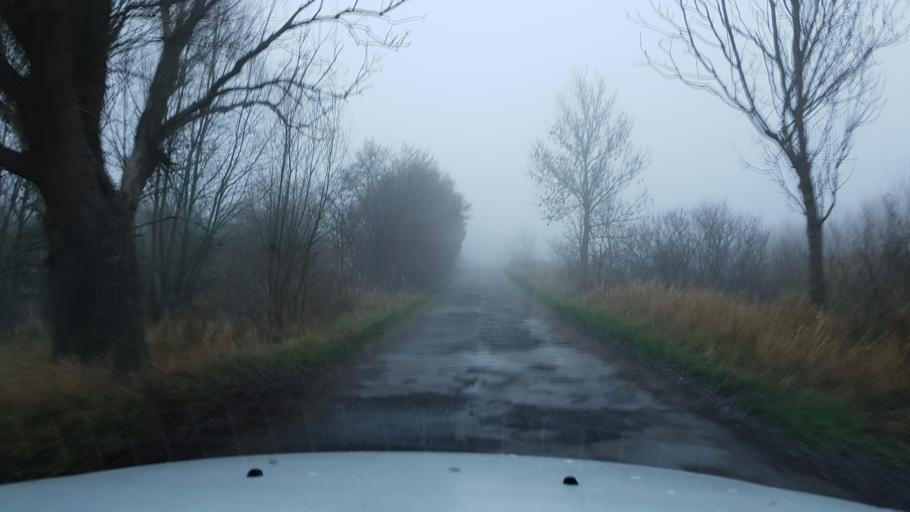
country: PL
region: West Pomeranian Voivodeship
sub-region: Powiat mysliborski
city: Mysliborz
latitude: 52.9454
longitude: 14.7916
